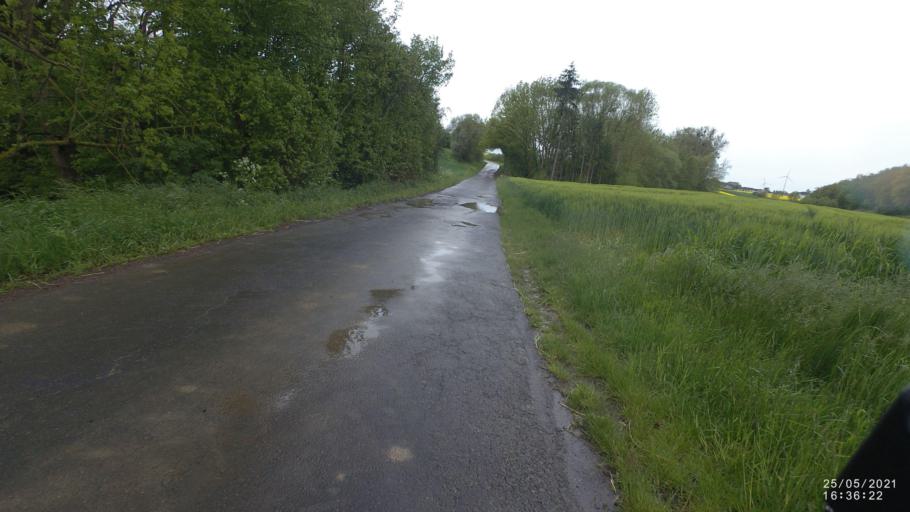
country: DE
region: Rheinland-Pfalz
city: Mayen
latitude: 50.3090
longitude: 7.2369
